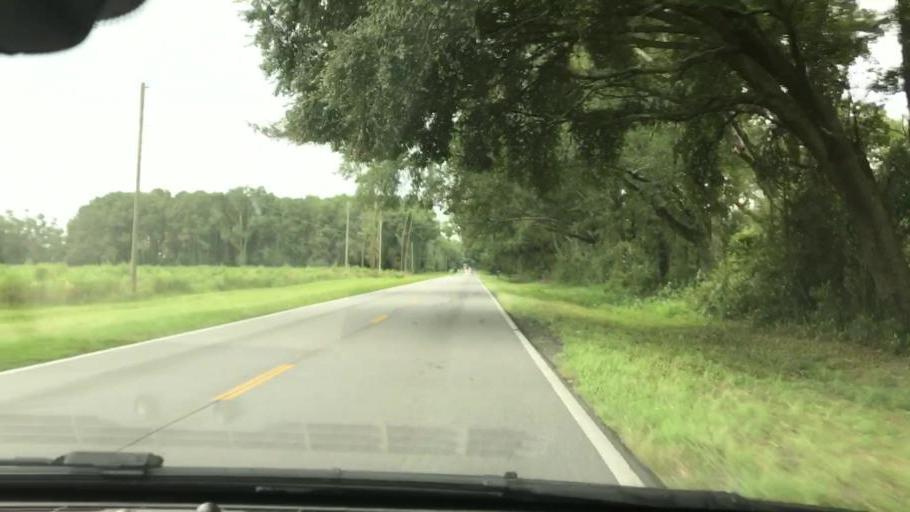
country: US
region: Florida
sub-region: Madison County
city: Madison
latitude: 30.4057
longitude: -83.3004
